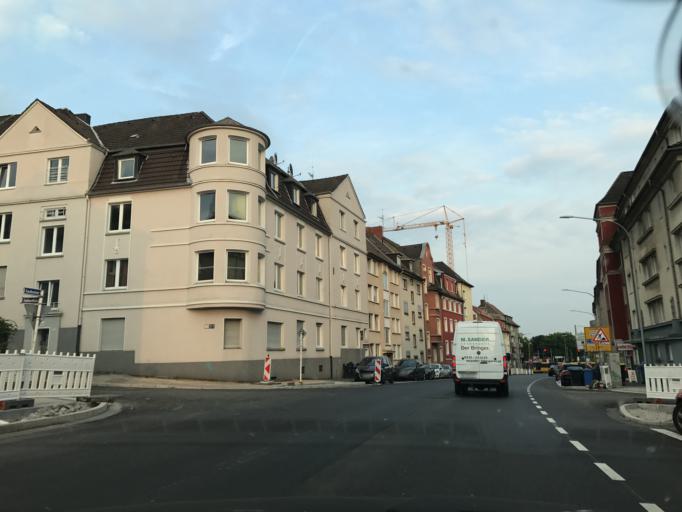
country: DE
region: North Rhine-Westphalia
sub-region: Regierungsbezirk Dusseldorf
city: Essen
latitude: 51.4377
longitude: 6.9852
